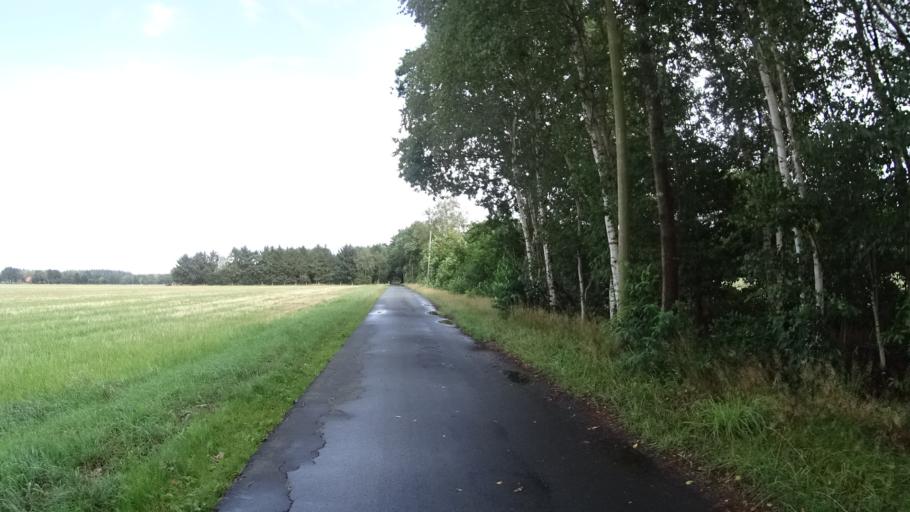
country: DE
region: Lower Saxony
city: Friedeburg
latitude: 53.3843
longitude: 7.8748
